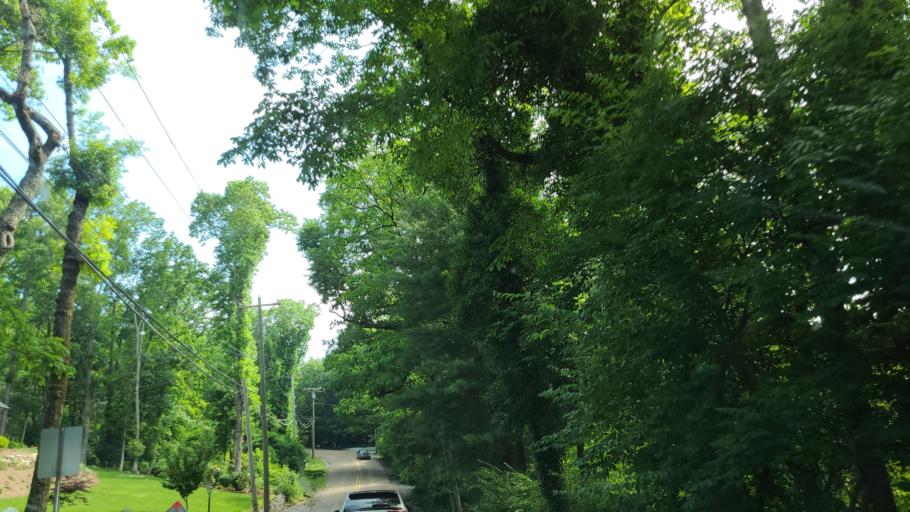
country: US
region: Tennessee
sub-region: Hamilton County
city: Lookout Mountain
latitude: 35.0003
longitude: -85.3464
